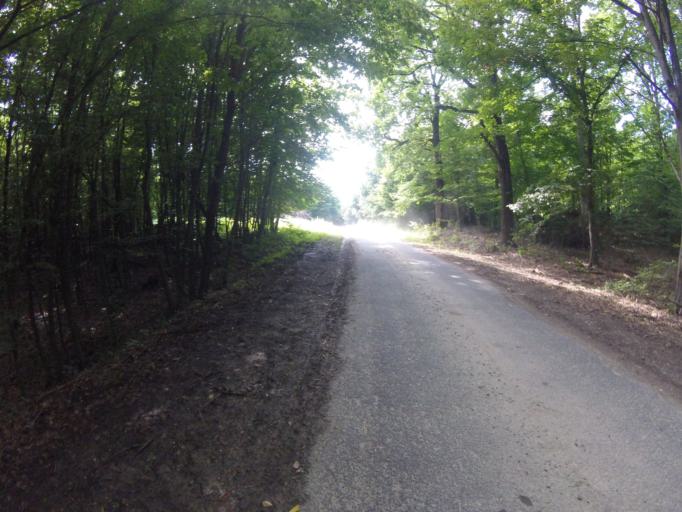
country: HR
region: Medimurska
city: Podturen
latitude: 46.5457
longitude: 16.6235
